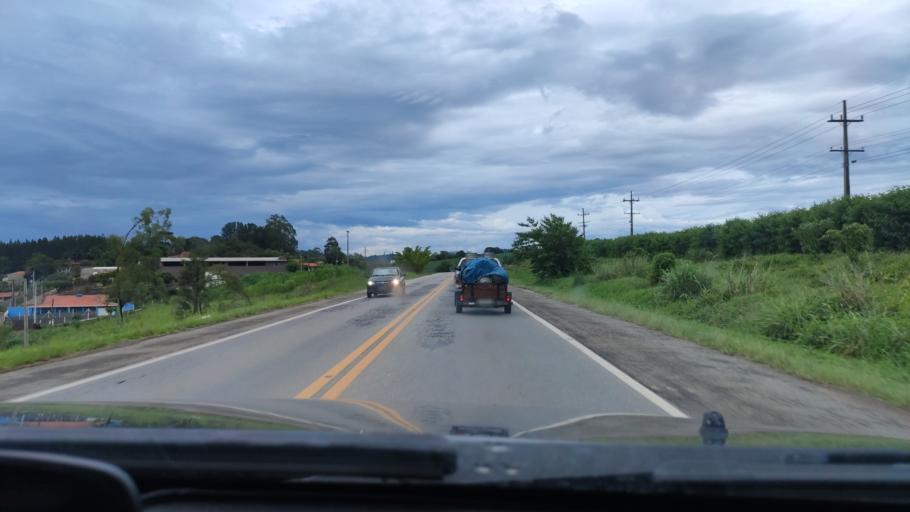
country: BR
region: Sao Paulo
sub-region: Braganca Paulista
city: Braganca Paulista
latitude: -22.8634
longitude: -46.5375
